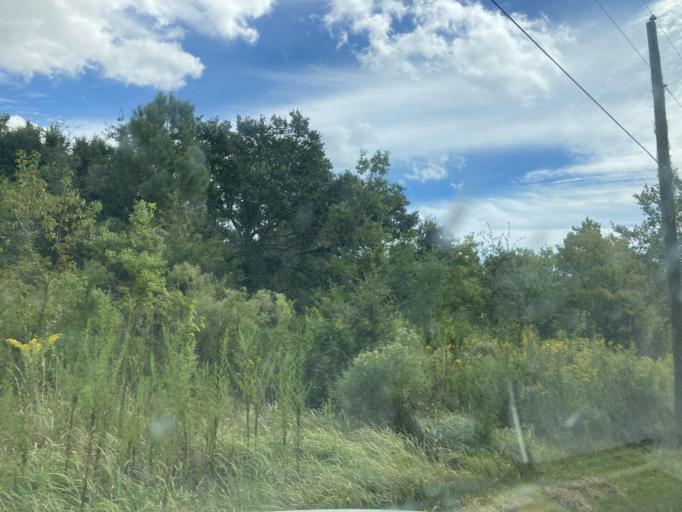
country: US
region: Mississippi
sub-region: Harrison County
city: D'Iberville
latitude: 30.4312
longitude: -88.8829
